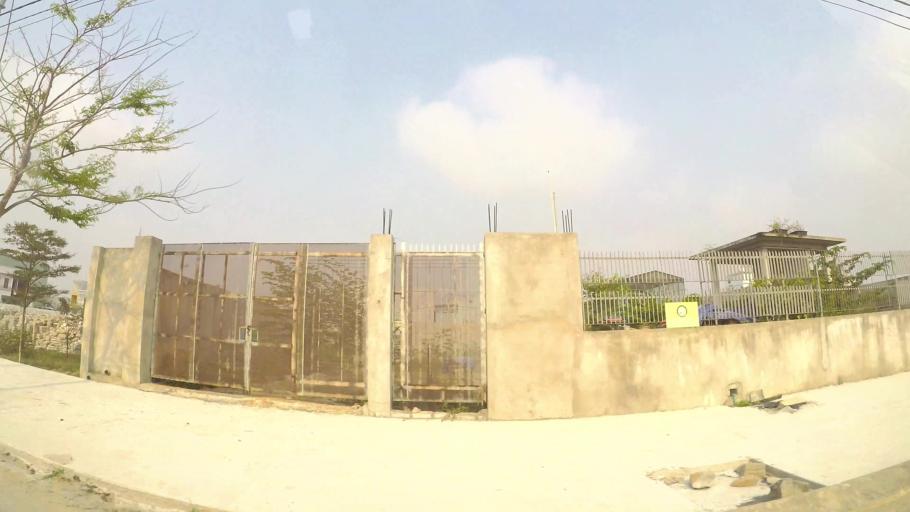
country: VN
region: Da Nang
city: Ngu Hanh Son
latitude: 16.0079
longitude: 108.2306
